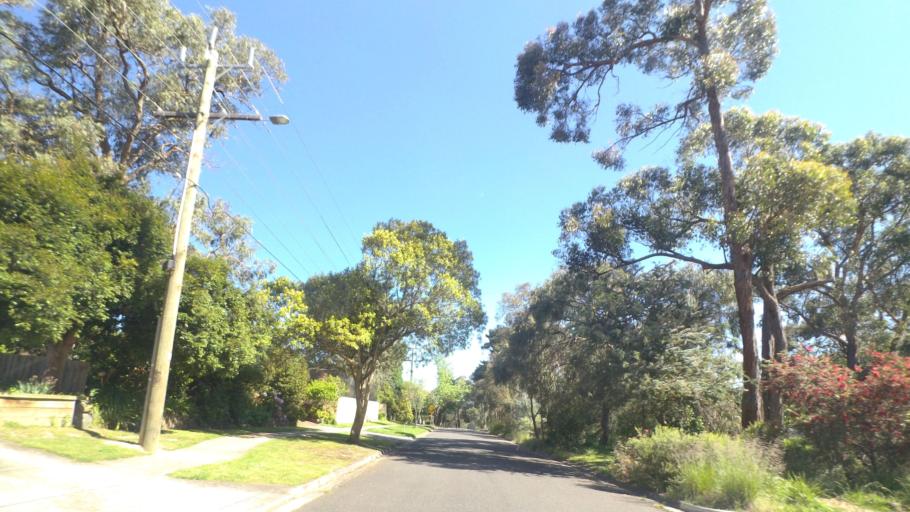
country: AU
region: Victoria
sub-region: Maroondah
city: Heathmont
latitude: -37.8311
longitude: 145.2492
